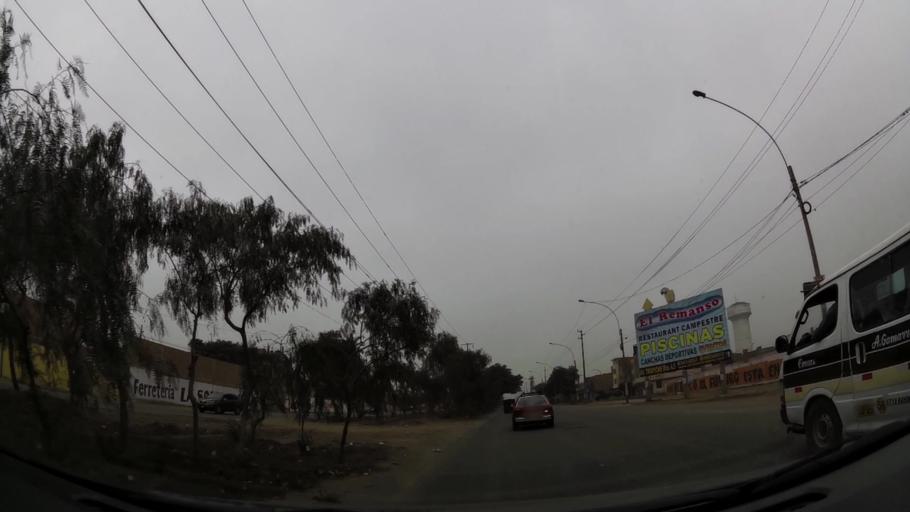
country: PE
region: Lima
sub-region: Lima
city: Urb. Santo Domingo
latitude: -11.9099
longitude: -77.0556
